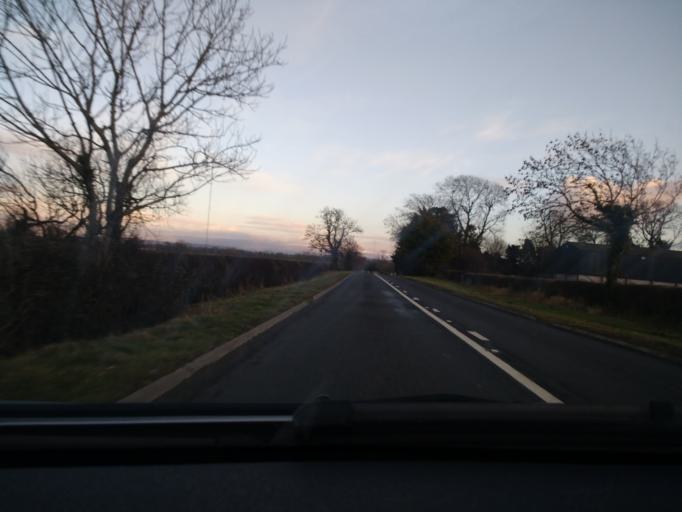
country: GB
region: England
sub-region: Cumbria
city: Scotby
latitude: 54.7295
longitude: -2.9171
